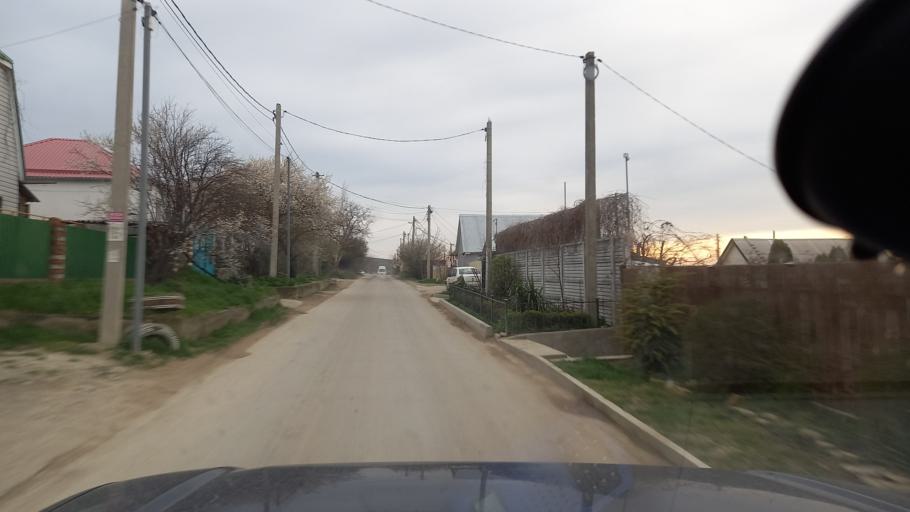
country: RU
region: Krasnodarskiy
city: Anapa
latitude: 44.8503
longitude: 37.3553
